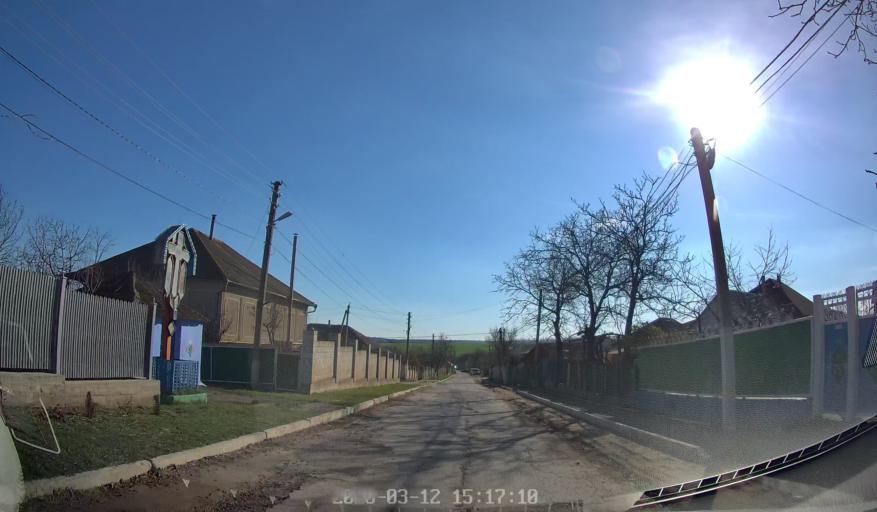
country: MD
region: Chisinau
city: Ciorescu
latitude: 47.2222
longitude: 28.9360
